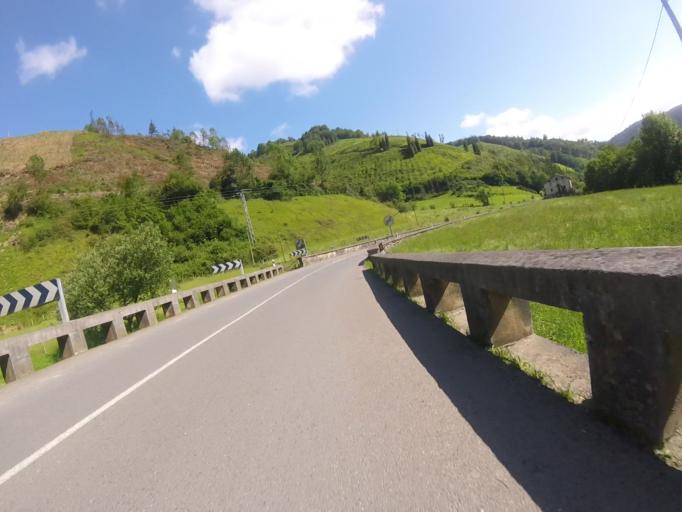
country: ES
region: Basque Country
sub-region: Provincia de Guipuzcoa
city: Beizama
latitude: 43.1097
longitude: -2.2397
